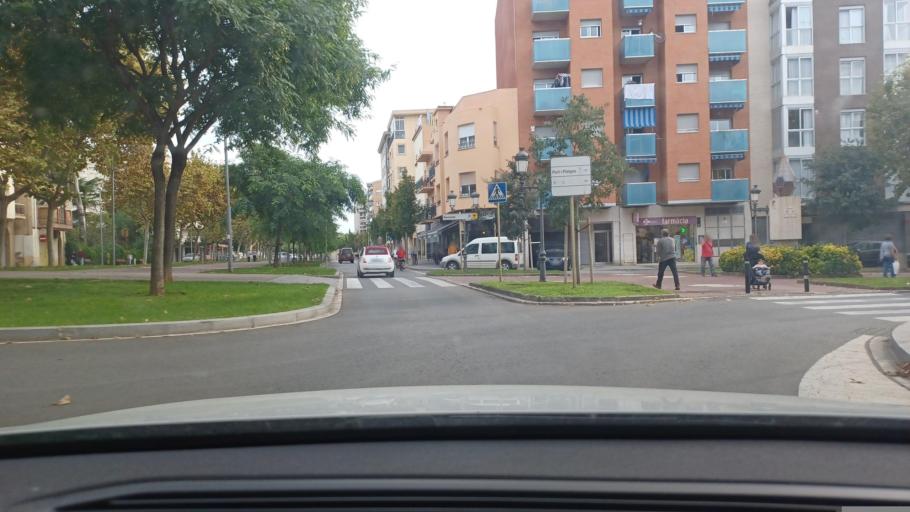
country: ES
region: Catalonia
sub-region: Provincia de Tarragona
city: Cambrils
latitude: 41.0712
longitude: 1.0521
